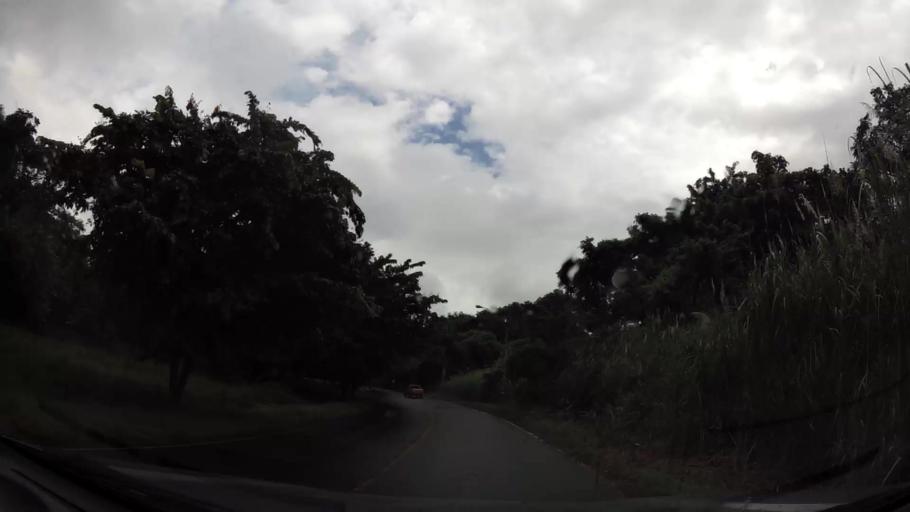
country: PA
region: Panama
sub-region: Distrito de Panama
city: Ancon
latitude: 8.9862
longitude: -79.5565
